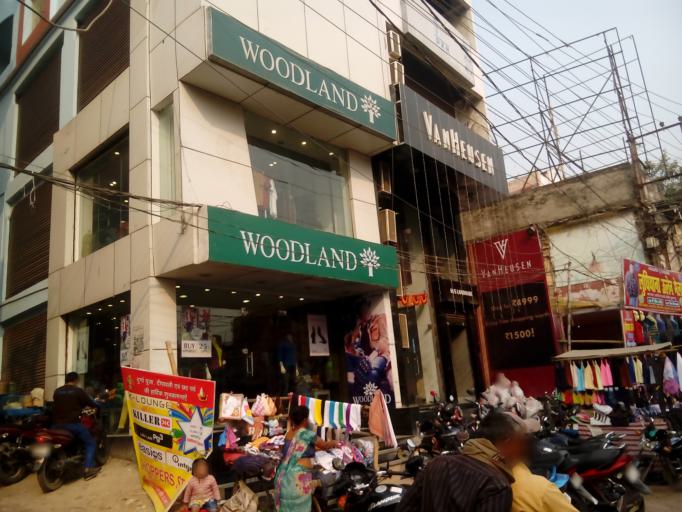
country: IN
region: Bihar
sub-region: Muzaffarpur
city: Muzaffarpur
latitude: 26.1194
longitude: 85.3885
